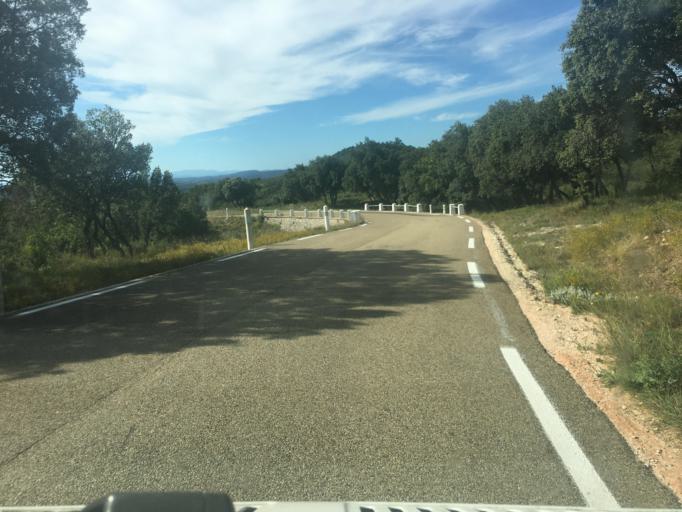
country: FR
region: Languedoc-Roussillon
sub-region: Departement du Gard
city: Saint-Quentin-la-Poterie
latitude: 44.0288
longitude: 4.5022
